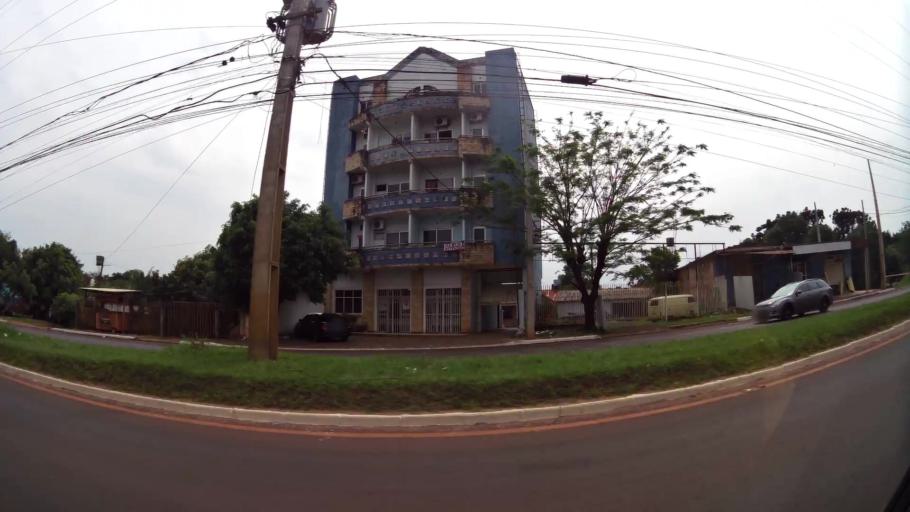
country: PY
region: Alto Parana
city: Presidente Franco
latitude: -25.5446
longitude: -54.6322
